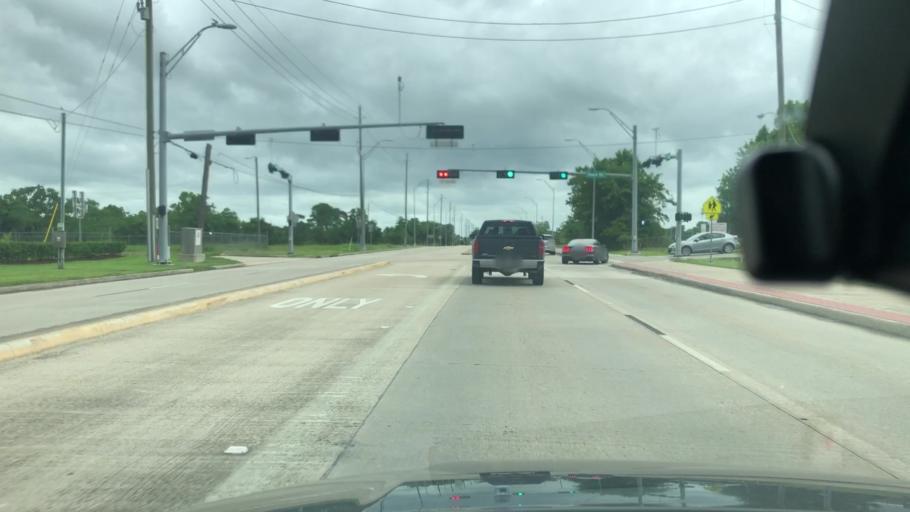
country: US
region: Texas
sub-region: Brazoria County
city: Brookside Village
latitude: 29.5768
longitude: -95.3509
